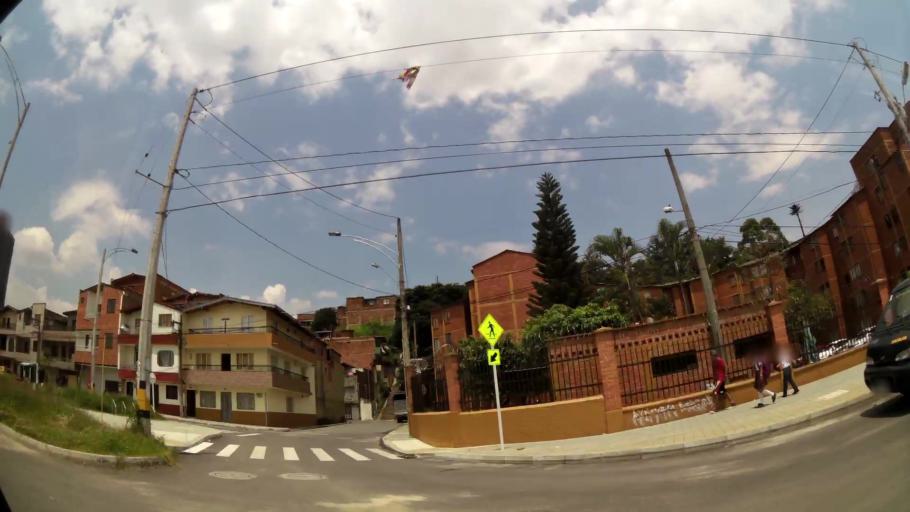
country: CO
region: Antioquia
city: Itagui
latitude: 6.1769
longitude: -75.6060
